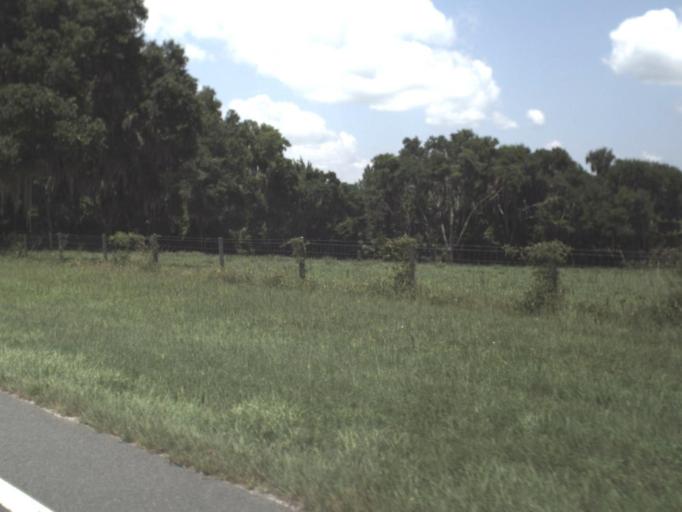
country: US
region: Florida
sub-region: Alachua County
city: Archer
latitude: 29.5130
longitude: -82.4064
